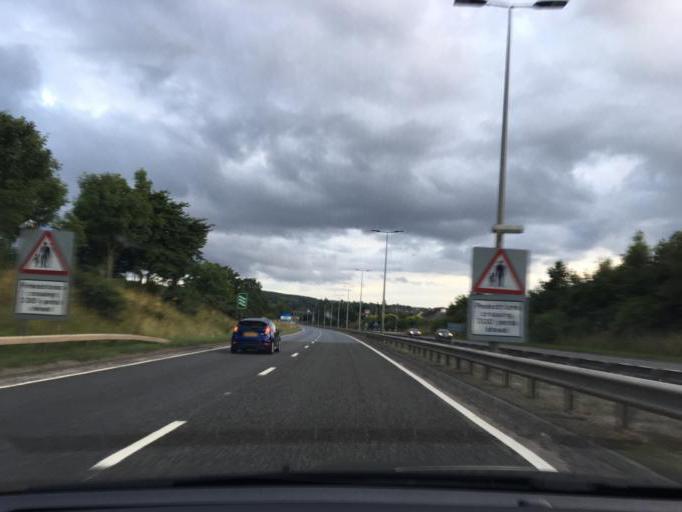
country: GB
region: Scotland
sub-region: Highland
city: Inverness
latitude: 57.4758
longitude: -4.1874
